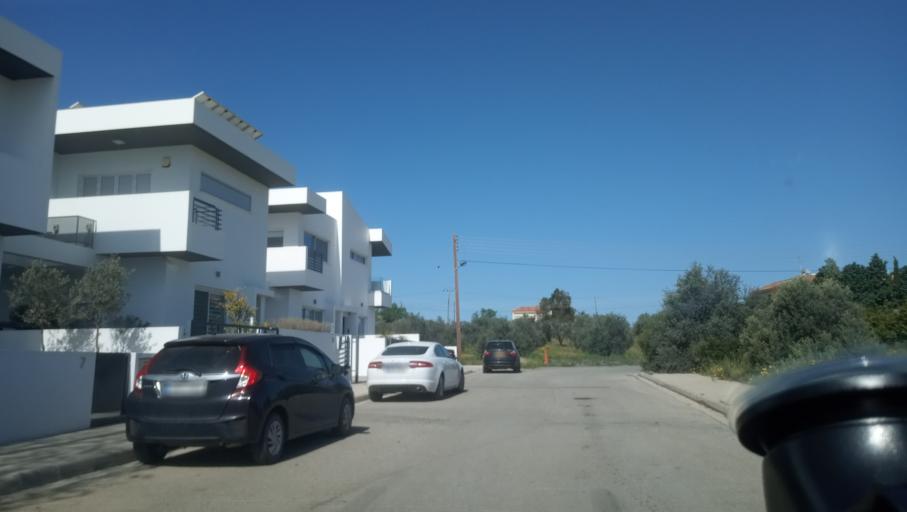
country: CY
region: Lefkosia
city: Tseri
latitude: 35.0909
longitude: 33.3057
